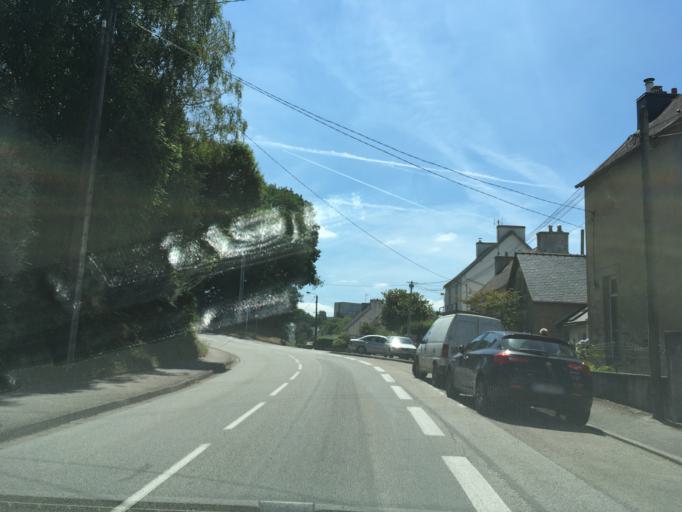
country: FR
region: Brittany
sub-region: Departement du Finistere
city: Quimper
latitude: 48.0054
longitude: -4.1058
